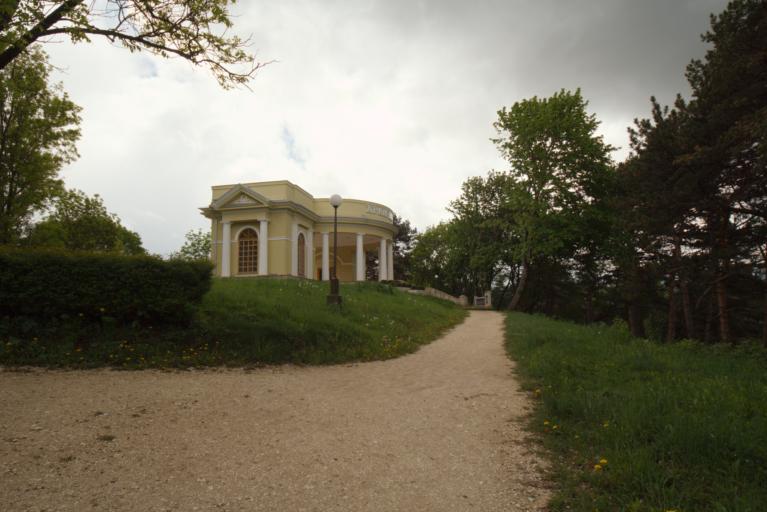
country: RU
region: Stavropol'skiy
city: Kislovodsk
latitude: 43.8975
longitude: 42.7365
